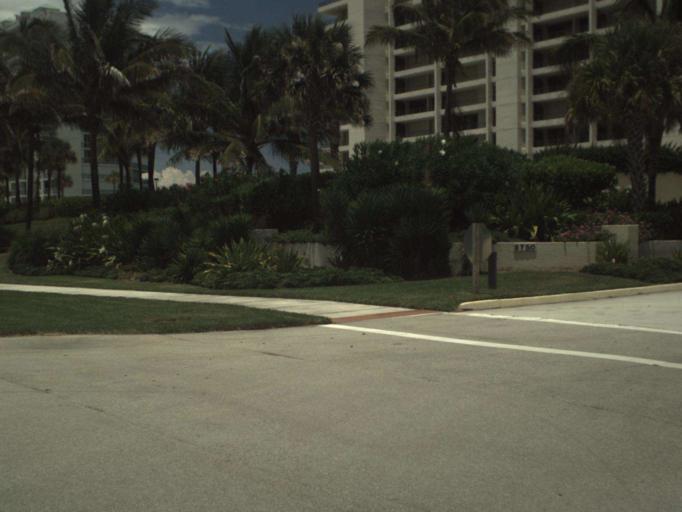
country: US
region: Florida
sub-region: Saint Lucie County
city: Hutchinson Island South
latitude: 27.3029
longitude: -80.2195
